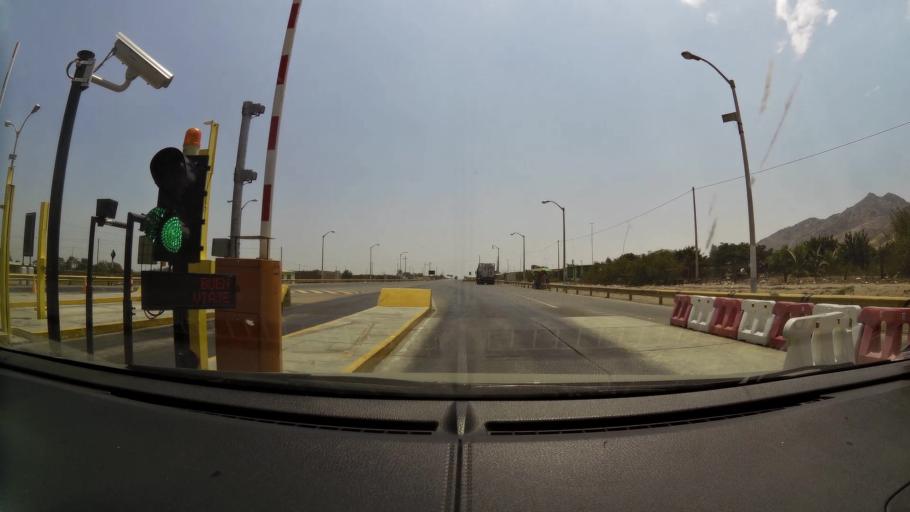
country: PE
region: La Libertad
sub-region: Chepen
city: Pacanga
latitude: -7.1117
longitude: -79.4969
